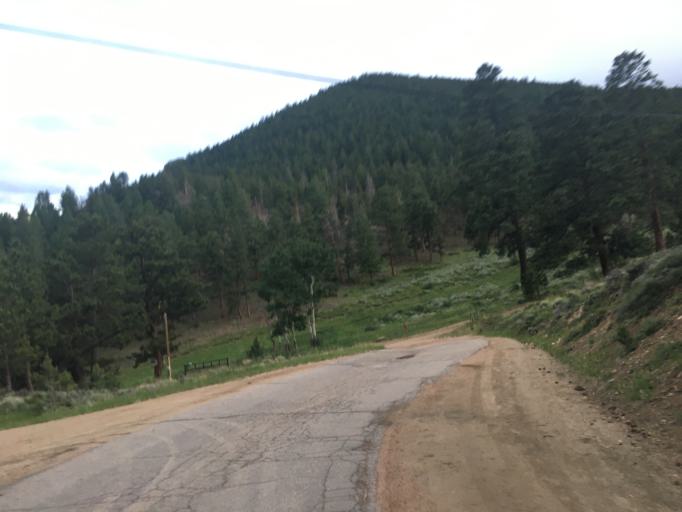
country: US
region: Colorado
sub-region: Larimer County
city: Estes Park
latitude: 40.3369
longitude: -105.5825
